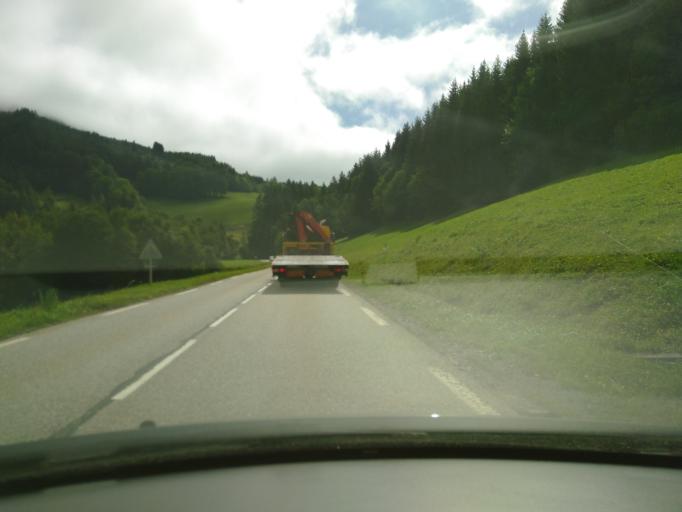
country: FR
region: Rhone-Alpes
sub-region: Departement de la Haute-Savoie
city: Saint-Jean-de-Sixt
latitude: 45.9283
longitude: 6.4066
